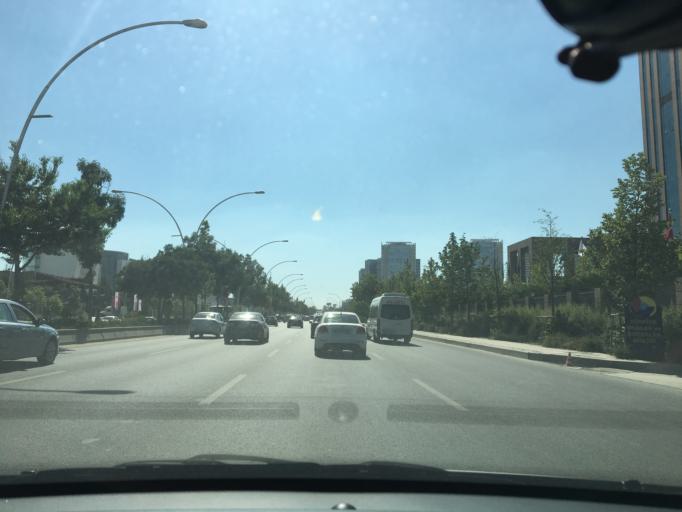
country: TR
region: Ankara
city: Batikent
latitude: 39.9078
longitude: 32.7627
